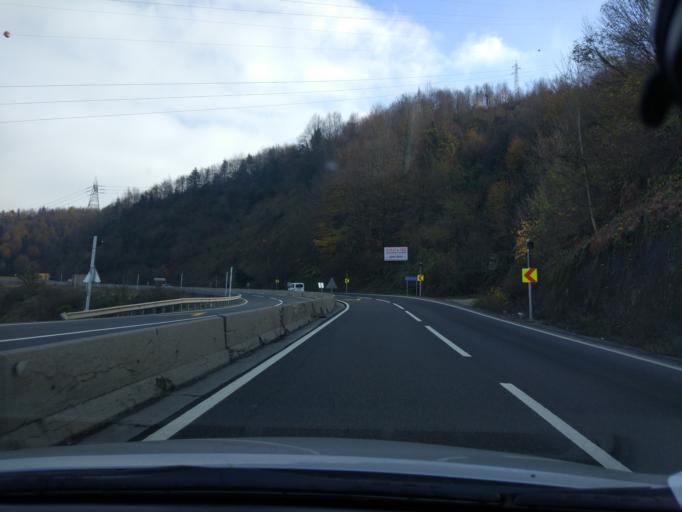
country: TR
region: Duzce
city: Kaynasli
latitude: 40.7524
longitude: 31.3853
